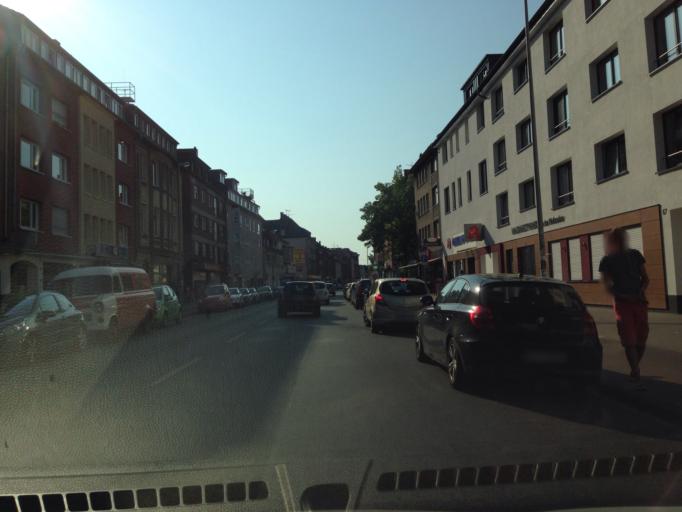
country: DE
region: North Rhine-Westphalia
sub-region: Regierungsbezirk Munster
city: Muenster
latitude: 51.9566
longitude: 7.6424
